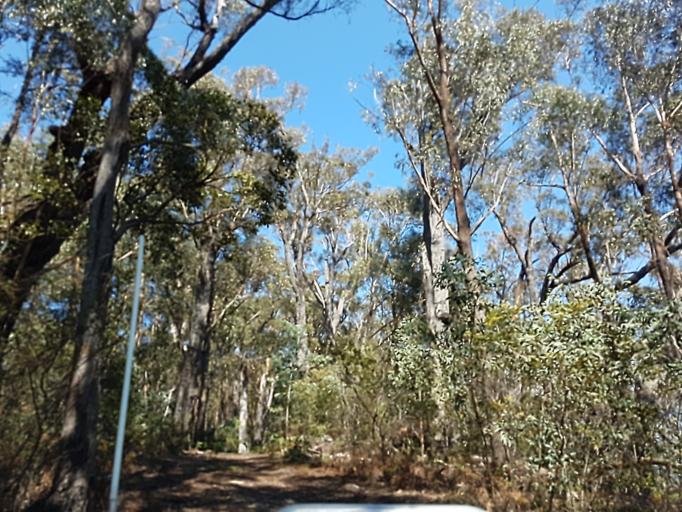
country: AU
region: Victoria
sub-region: East Gippsland
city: Lakes Entrance
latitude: -37.2892
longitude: 148.3261
